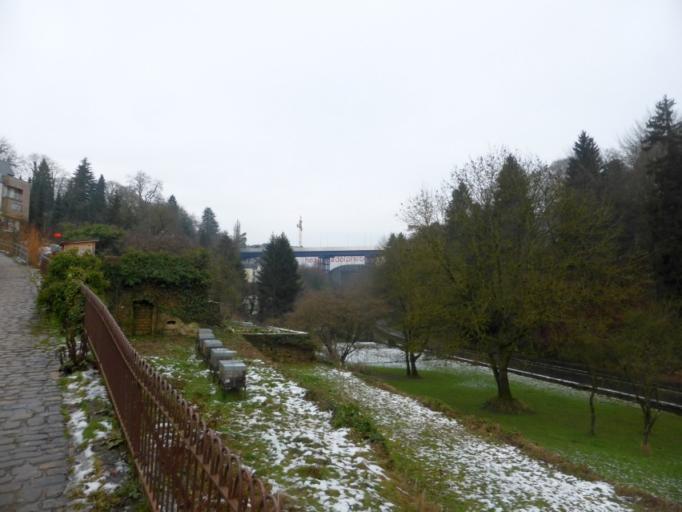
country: LU
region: Luxembourg
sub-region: Canton de Luxembourg
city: Luxembourg
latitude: 49.6059
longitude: 6.1233
